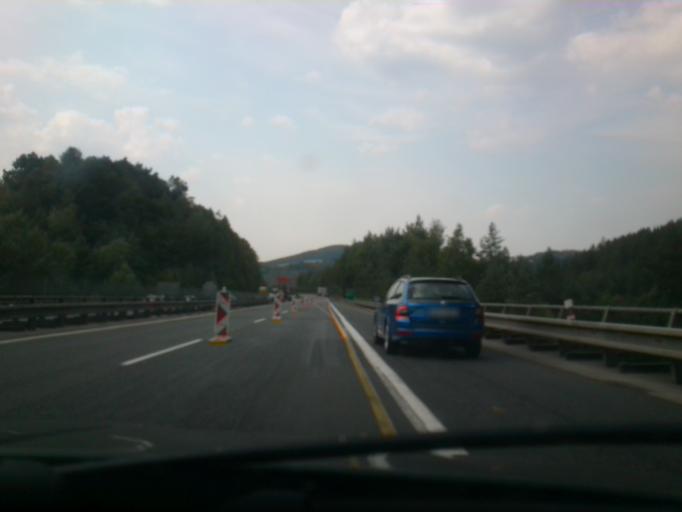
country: CZ
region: Central Bohemia
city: Ondrejov
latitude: 49.8648
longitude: 14.7856
